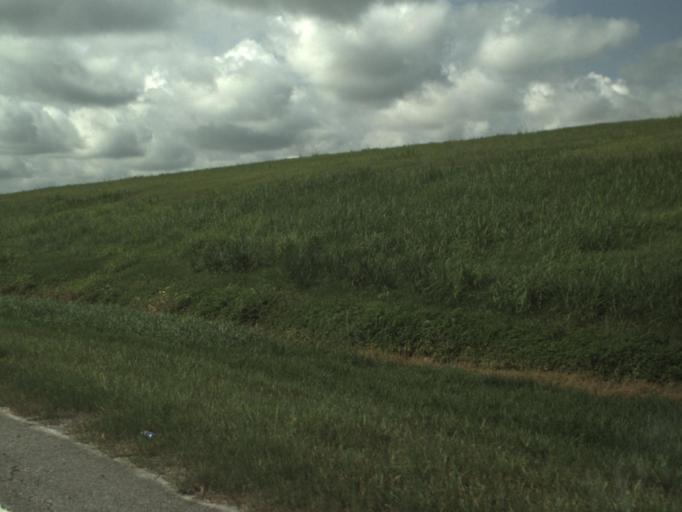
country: US
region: Florida
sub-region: Palm Beach County
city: Pahokee
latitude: 26.7620
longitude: -80.6870
